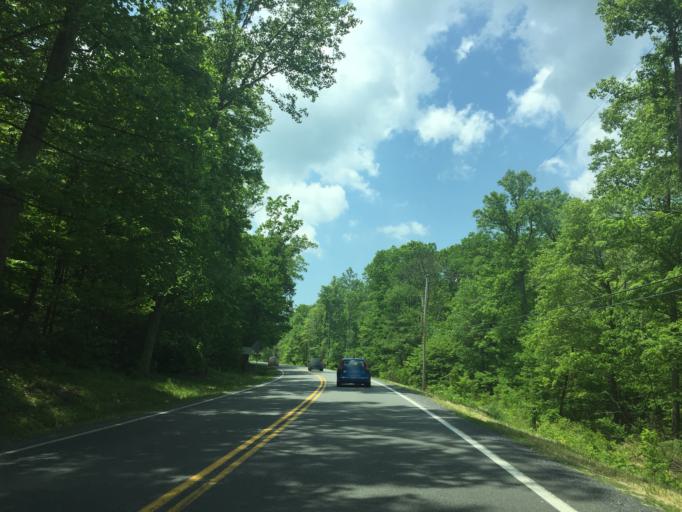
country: US
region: Virginia
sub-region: Frederick County
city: Shawnee Land
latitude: 39.1000
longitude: -78.4770
